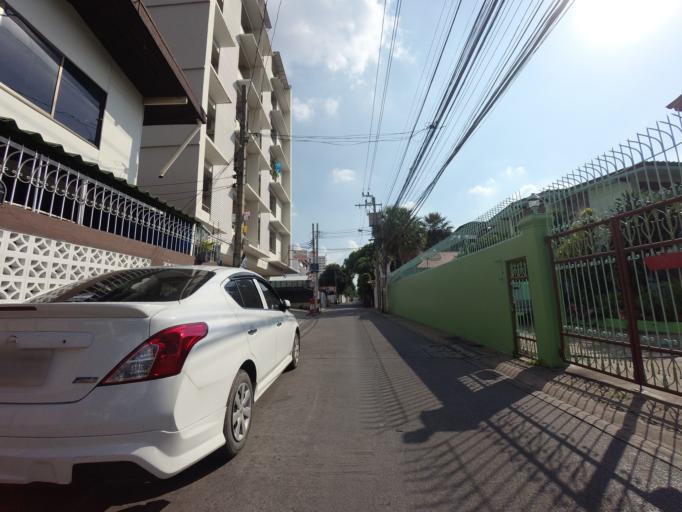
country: TH
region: Bangkok
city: Phaya Thai
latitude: 13.7885
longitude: 100.5556
